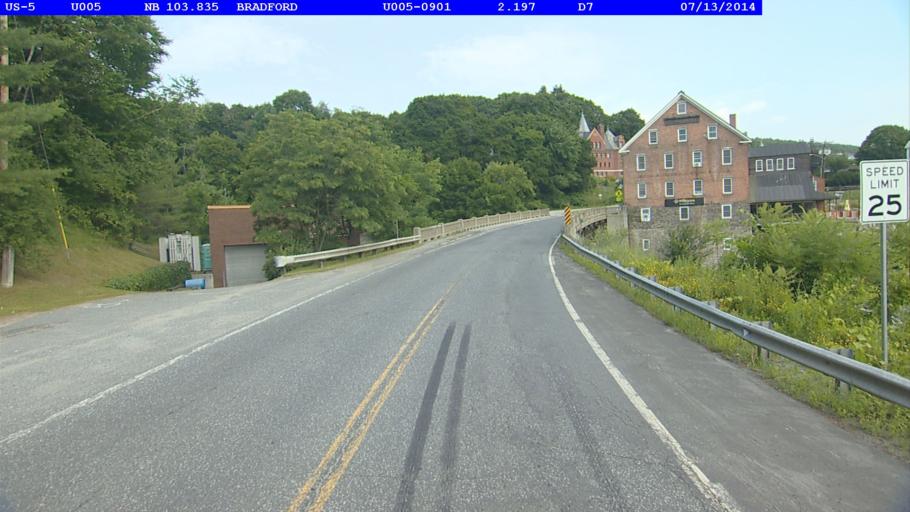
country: US
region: New Hampshire
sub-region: Grafton County
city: Haverhill
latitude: 43.9917
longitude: -72.1278
